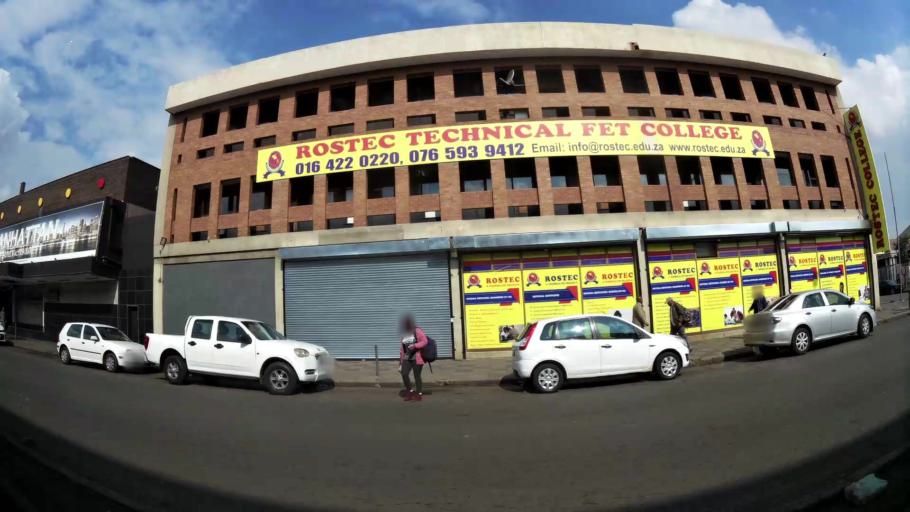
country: ZA
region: Gauteng
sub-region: Sedibeng District Municipality
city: Vereeniging
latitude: -26.6761
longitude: 27.9300
